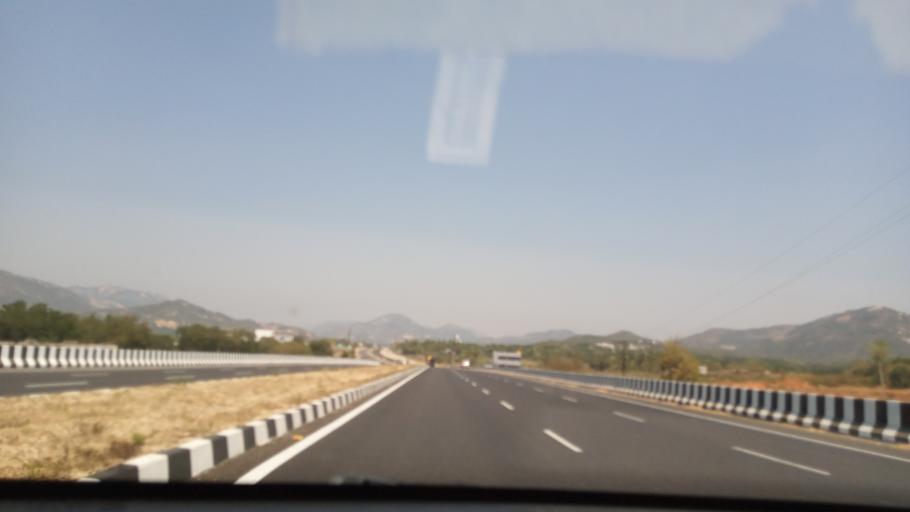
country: IN
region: Andhra Pradesh
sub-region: Chittoor
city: Pakala
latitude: 13.4536
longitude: 79.1617
